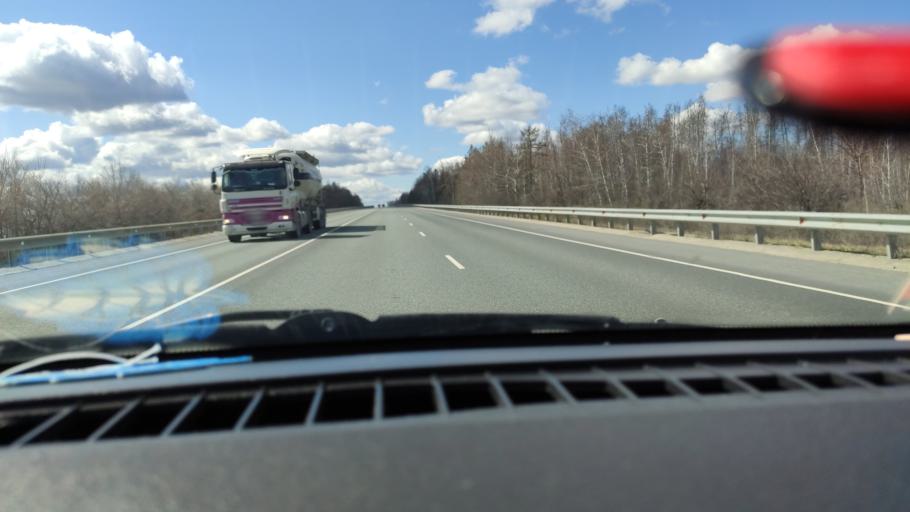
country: RU
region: Saratov
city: Khvalynsk
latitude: 52.5604
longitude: 48.0886
